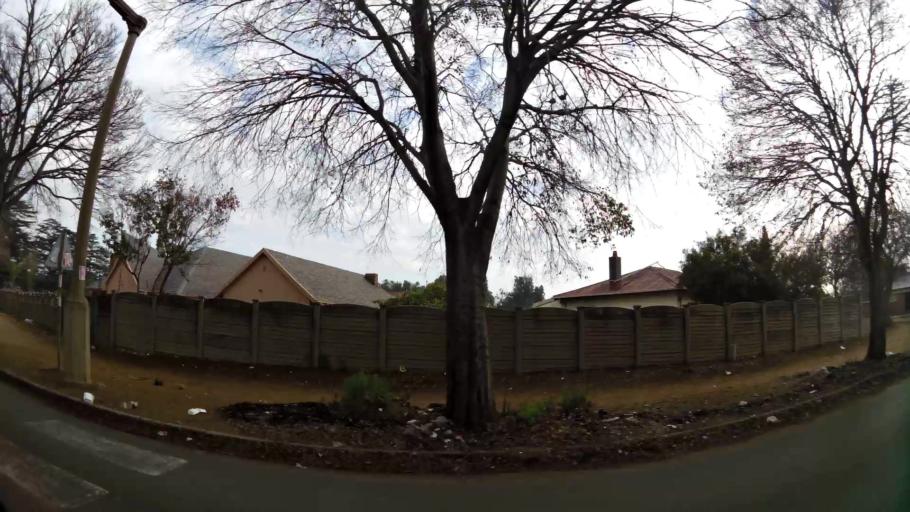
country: ZA
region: Gauteng
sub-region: Sedibeng District Municipality
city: Vanderbijlpark
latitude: -26.6887
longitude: 27.8140
